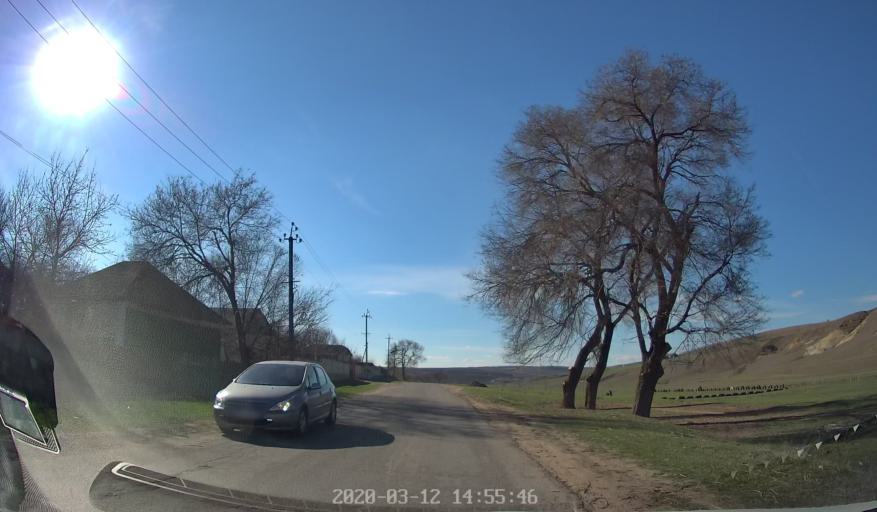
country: MD
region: Telenesti
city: Cocieri
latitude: 47.2243
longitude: 29.0578
